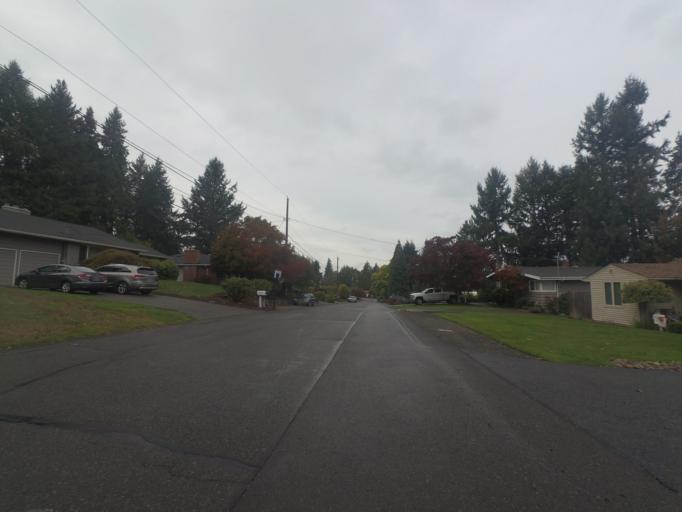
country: US
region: Washington
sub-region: Pierce County
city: University Place
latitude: 47.2181
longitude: -122.5593
